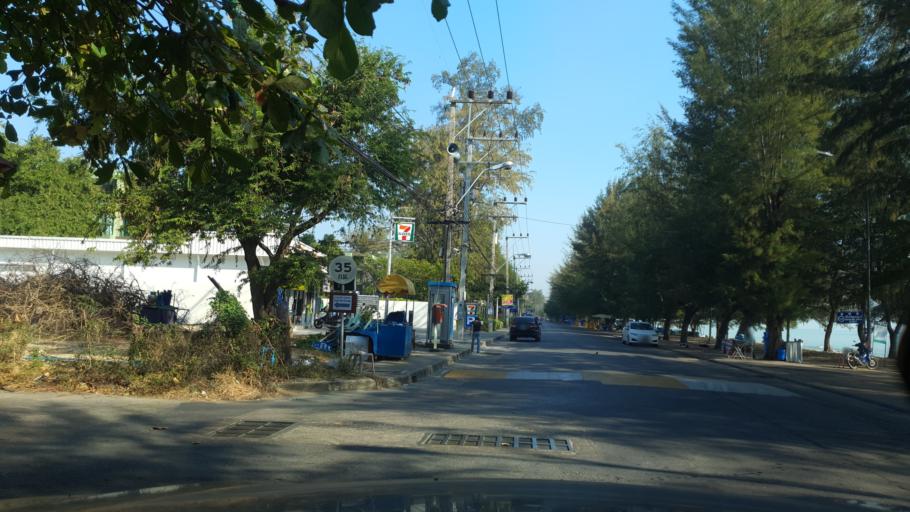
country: TH
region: Phetchaburi
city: Cha-am
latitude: 12.7780
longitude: 99.9775
